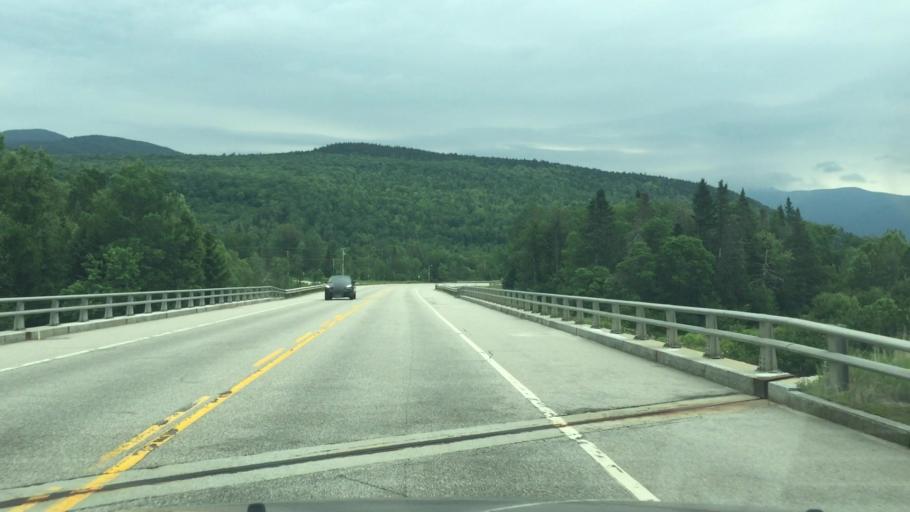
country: US
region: New Hampshire
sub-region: Grafton County
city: Deerfield
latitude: 44.2692
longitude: -71.4761
